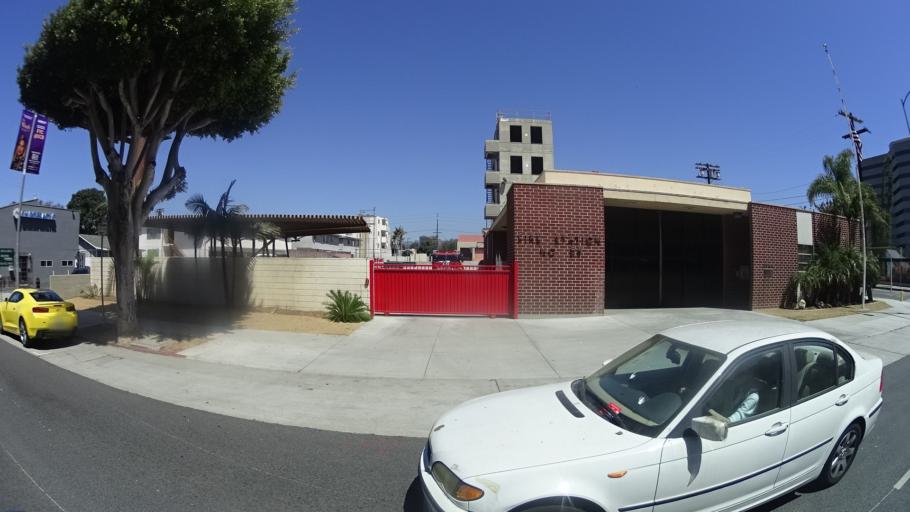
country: US
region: California
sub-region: Los Angeles County
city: Westwood, Los Angeles
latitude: 34.0364
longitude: -118.4445
